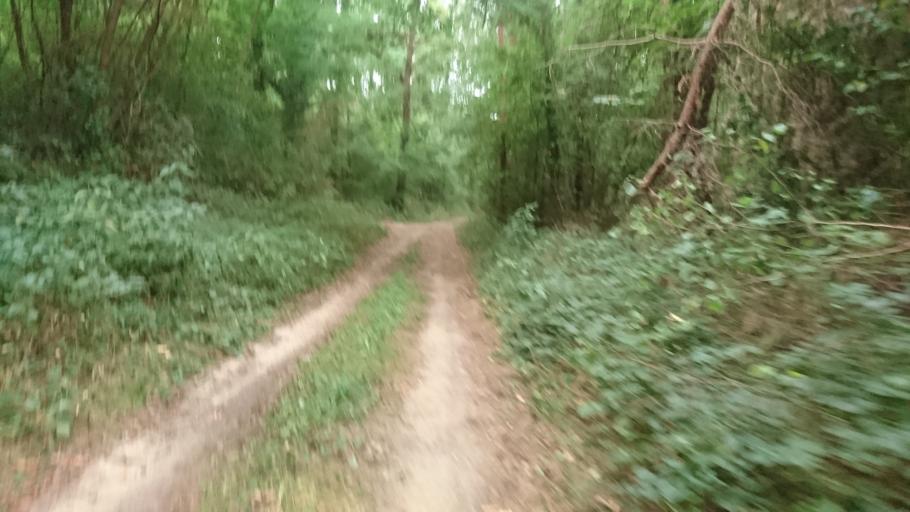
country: FR
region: Bourgogne
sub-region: Departement de l'Yonne
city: Fleury-la-Vallee
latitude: 47.8643
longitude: 3.4038
